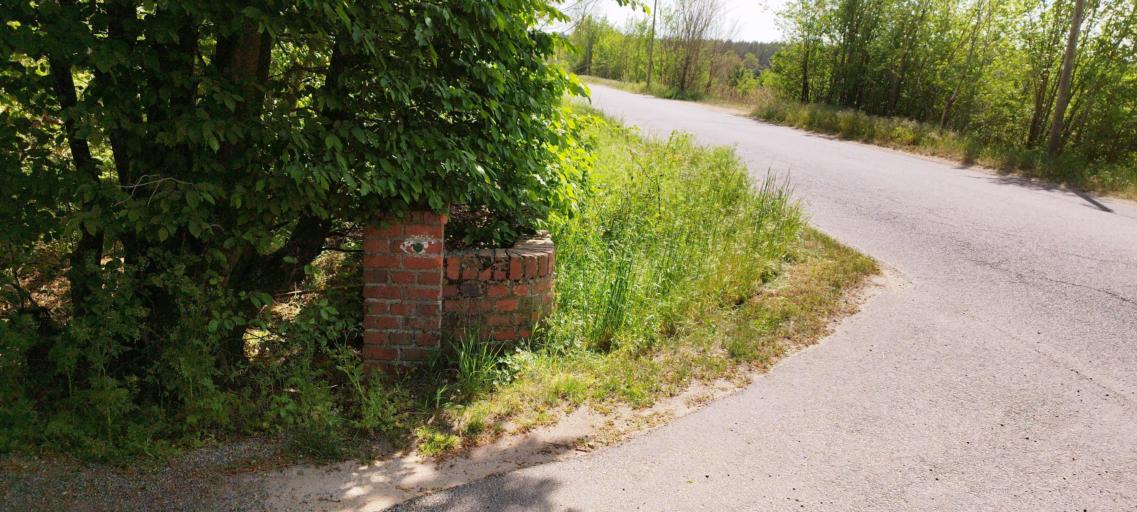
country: DE
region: Brandenburg
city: Rauen
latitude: 52.3752
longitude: 14.0107
